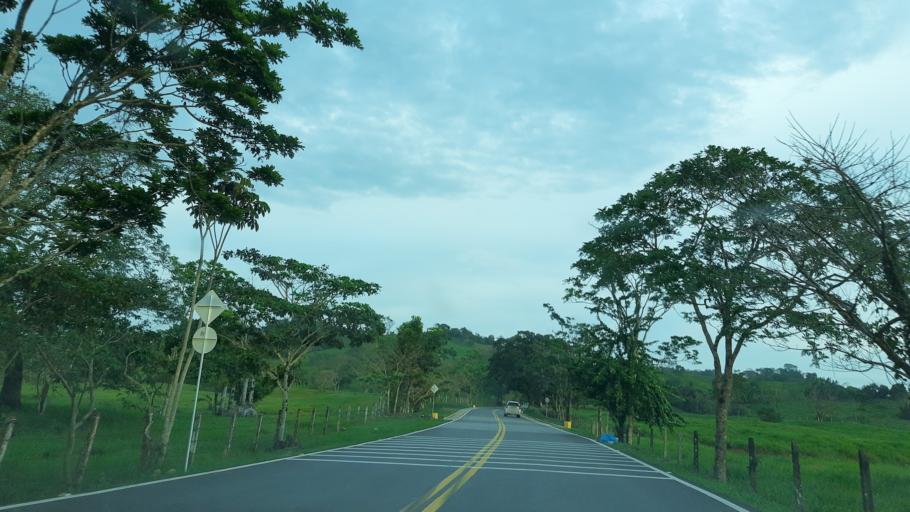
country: CO
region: Casanare
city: Sabanalarga
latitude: 4.7962
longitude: -73.0574
